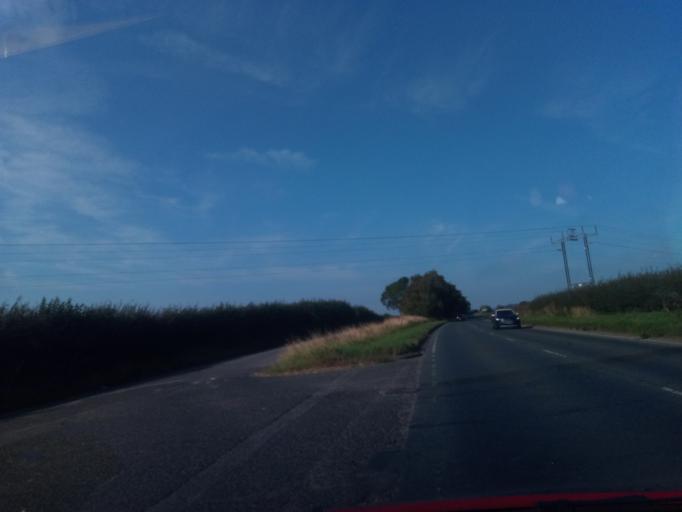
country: GB
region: England
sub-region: North Yorkshire
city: Raskelf
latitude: 54.1462
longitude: -1.2389
